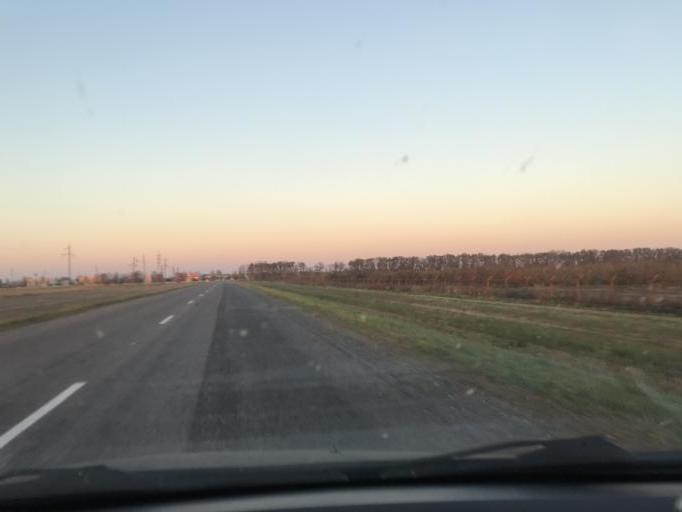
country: BY
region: Gomel
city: Loyew
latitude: 52.1408
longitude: 30.6013
